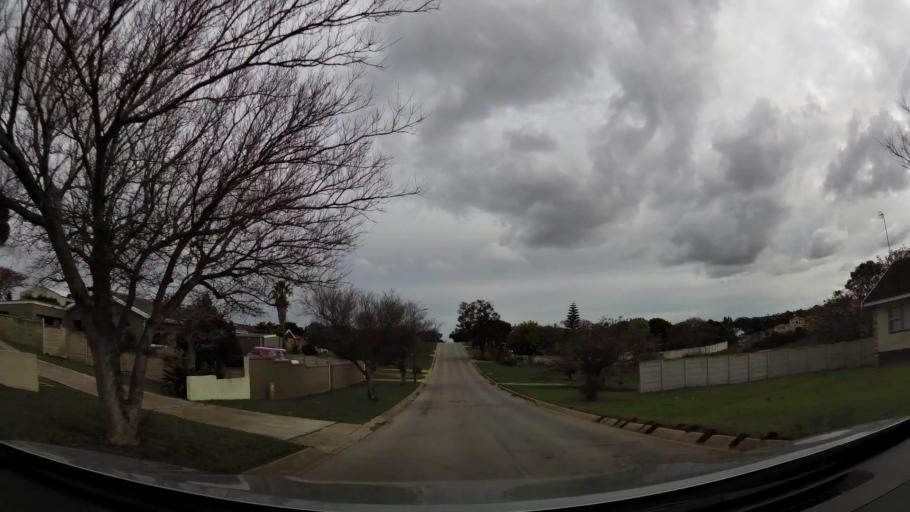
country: ZA
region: Eastern Cape
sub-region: Nelson Mandela Bay Metropolitan Municipality
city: Port Elizabeth
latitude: -33.9345
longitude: 25.5238
